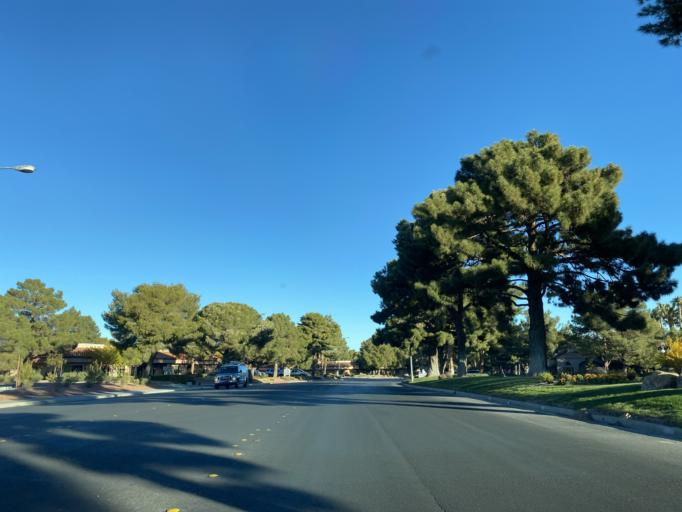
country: US
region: Nevada
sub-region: Clark County
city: Whitney
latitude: 36.0723
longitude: -115.1127
